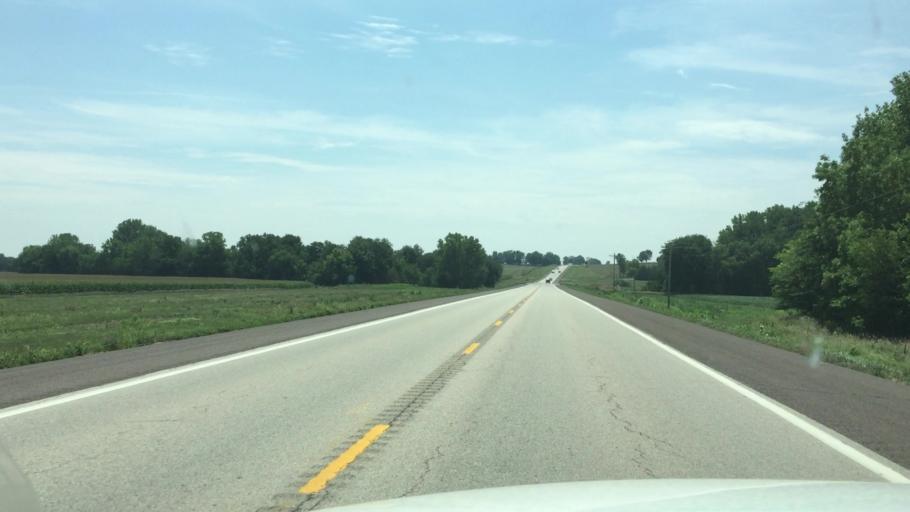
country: US
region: Kansas
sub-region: Jackson County
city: Holton
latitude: 39.5793
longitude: -95.7323
